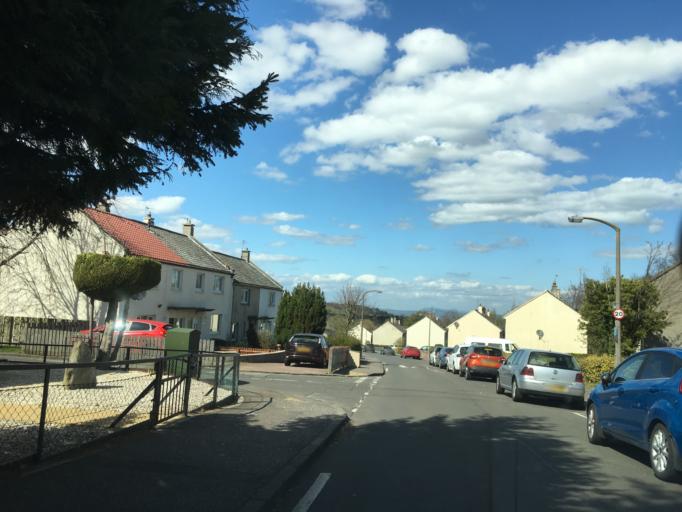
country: GB
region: Scotland
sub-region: Edinburgh
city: Colinton
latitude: 55.9044
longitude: -3.2188
